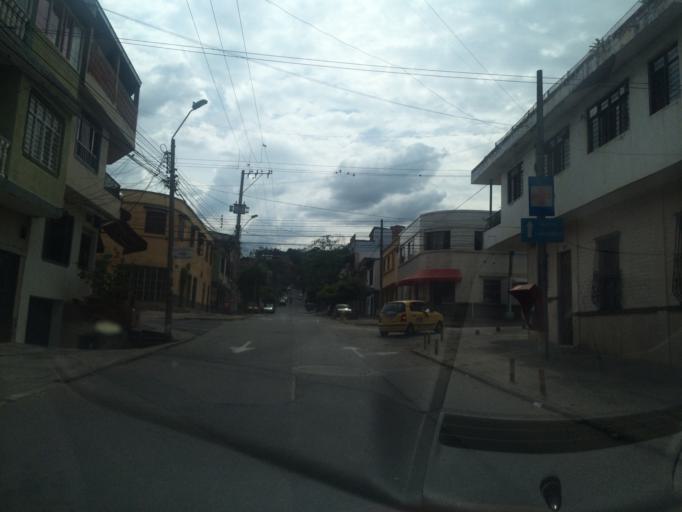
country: CO
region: Valle del Cauca
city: Cali
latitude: 3.4444
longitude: -76.5400
